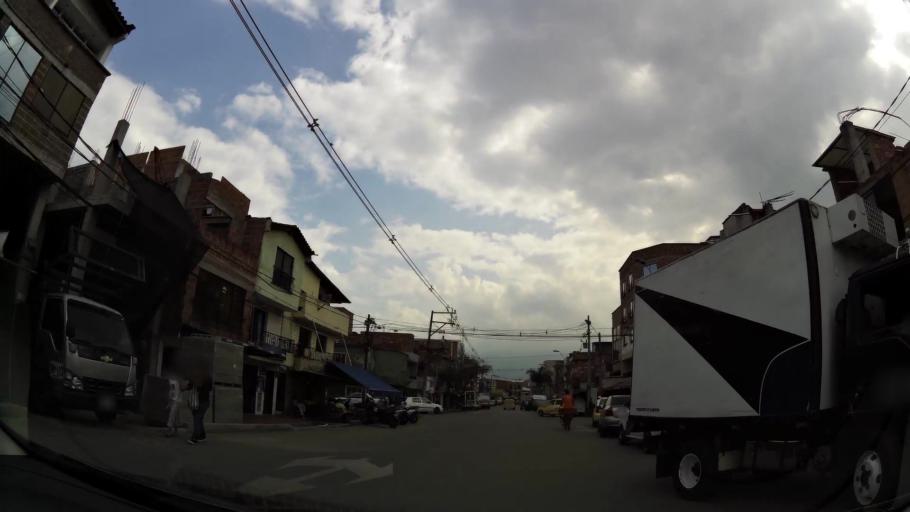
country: CO
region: Antioquia
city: Medellin
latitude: 6.2258
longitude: -75.5863
